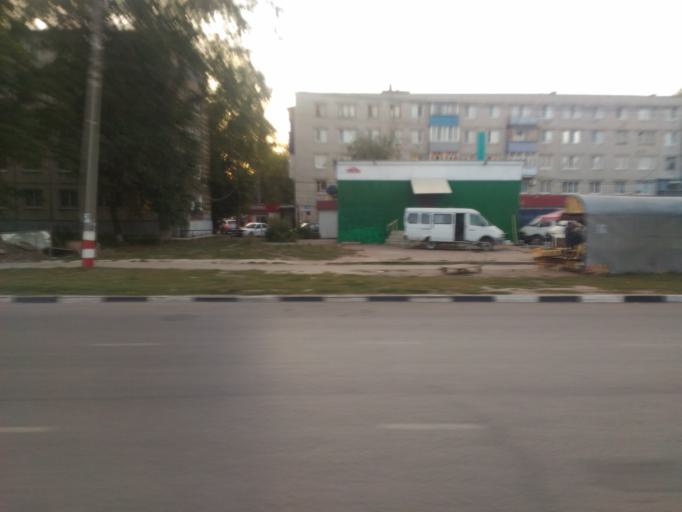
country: RU
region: Ulyanovsk
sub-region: Ulyanovskiy Rayon
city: Ulyanovsk
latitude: 54.2746
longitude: 48.2892
